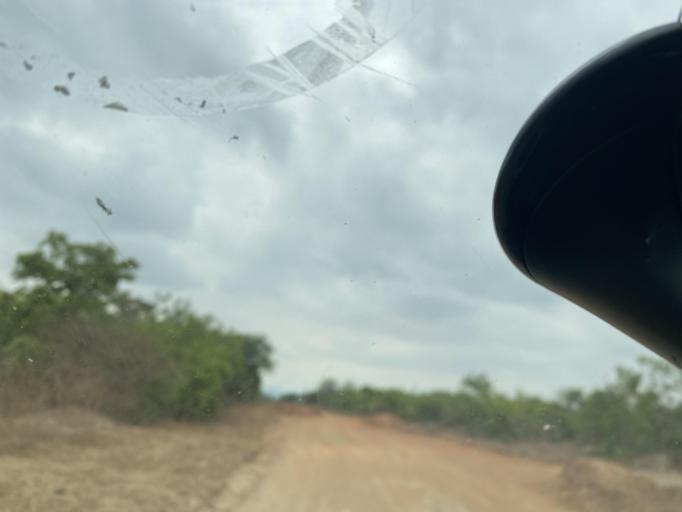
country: ZM
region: Lusaka
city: Chongwe
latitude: -15.2474
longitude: 28.7263
